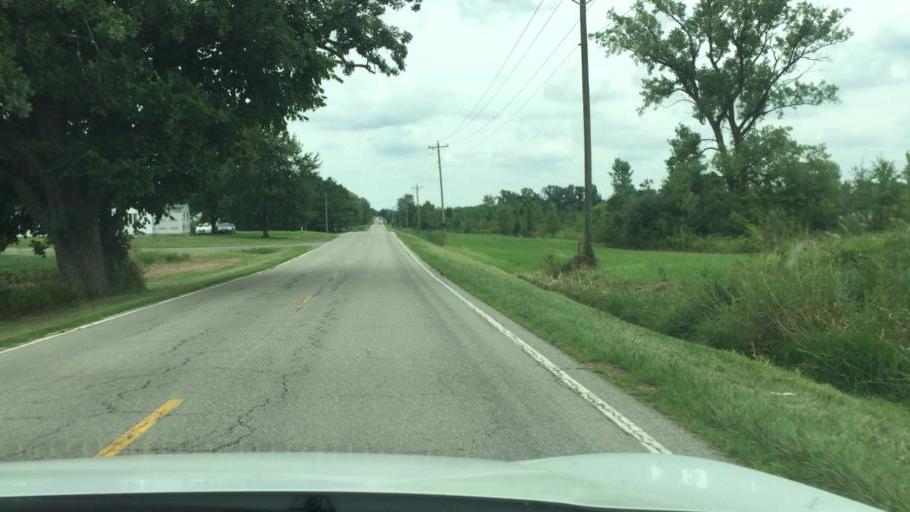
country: US
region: Ohio
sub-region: Champaign County
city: North Lewisburg
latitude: 40.2524
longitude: -83.4861
